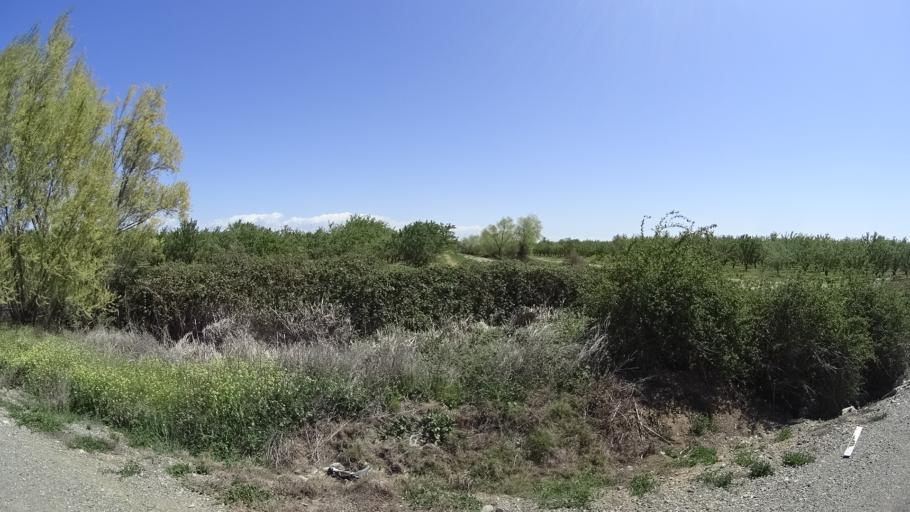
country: US
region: California
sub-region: Glenn County
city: Orland
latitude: 39.7904
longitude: -122.1410
